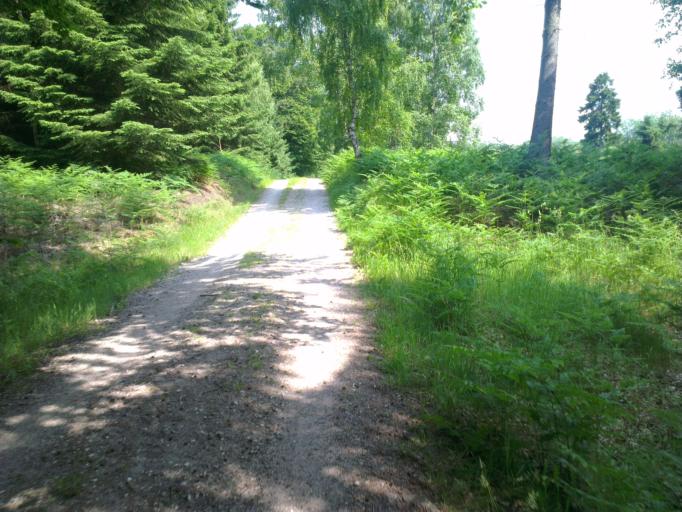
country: DK
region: Capital Region
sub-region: Allerod Kommune
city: Lillerod
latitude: 55.9102
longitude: 12.3578
